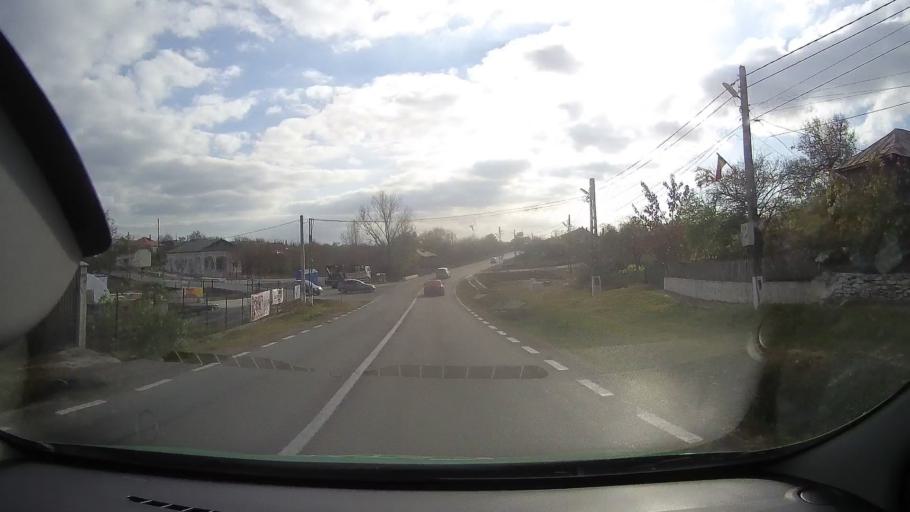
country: RO
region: Tulcea
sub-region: Comuna Topolog
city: Topolog
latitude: 44.8758
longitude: 28.3739
